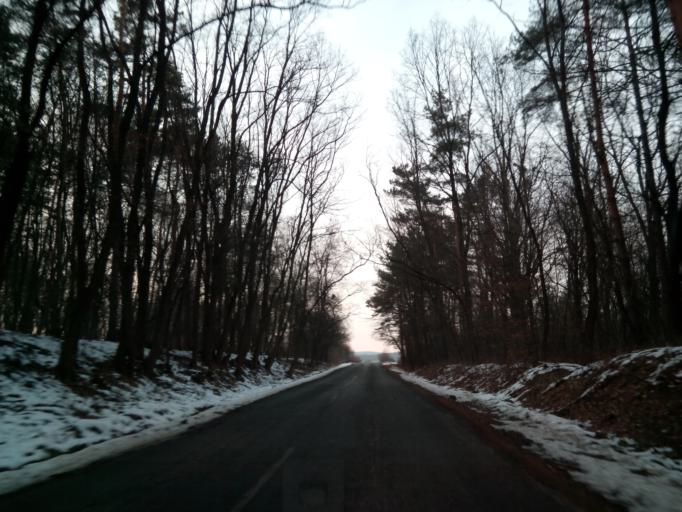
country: HU
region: Borsod-Abauj-Zemplen
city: Gonc
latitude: 48.4817
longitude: 21.3907
